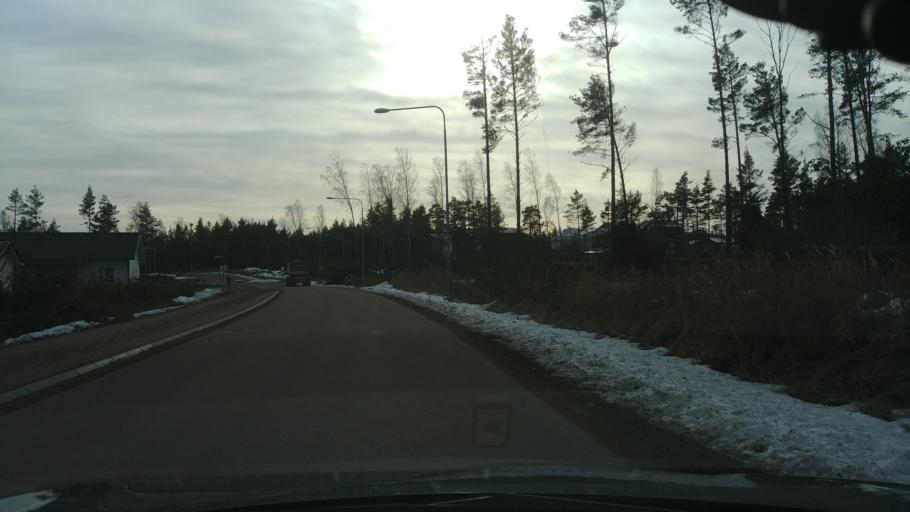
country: AX
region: Mariehamns stad
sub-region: Mariehamn
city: Mariehamn
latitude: 60.1013
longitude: 19.8928
